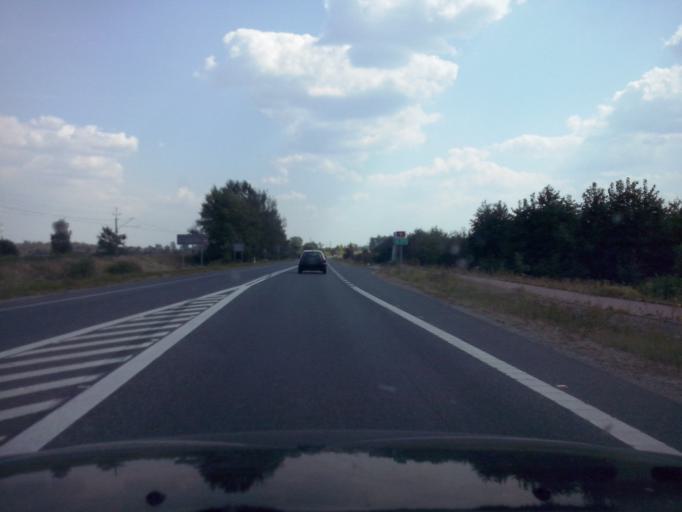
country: PL
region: Subcarpathian Voivodeship
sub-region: Powiat tarnobrzeski
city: Baranow Sandomierski
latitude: 50.5277
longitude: 21.5872
